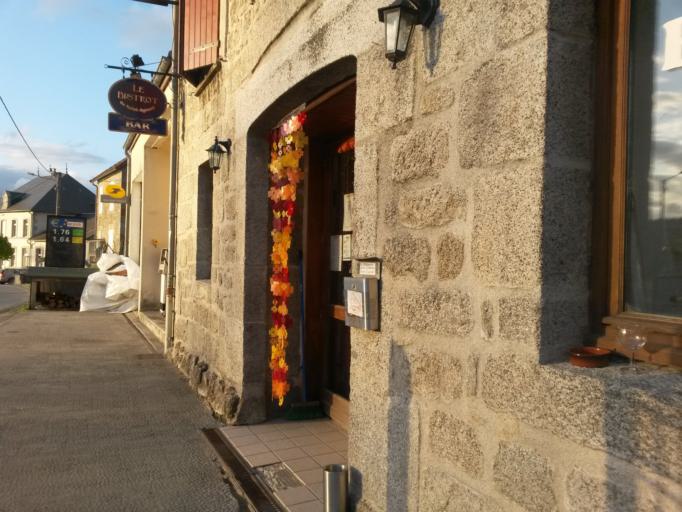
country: FR
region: Limousin
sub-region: Departement de la Creuse
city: La Courtine
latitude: 45.8040
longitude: 2.3502
